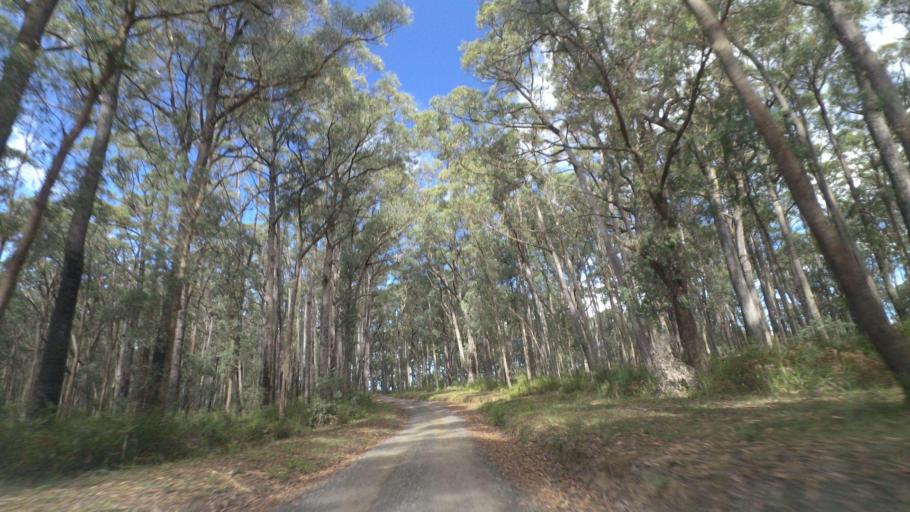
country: AU
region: Victoria
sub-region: Cardinia
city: Gembrook
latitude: -37.9143
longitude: 145.6022
